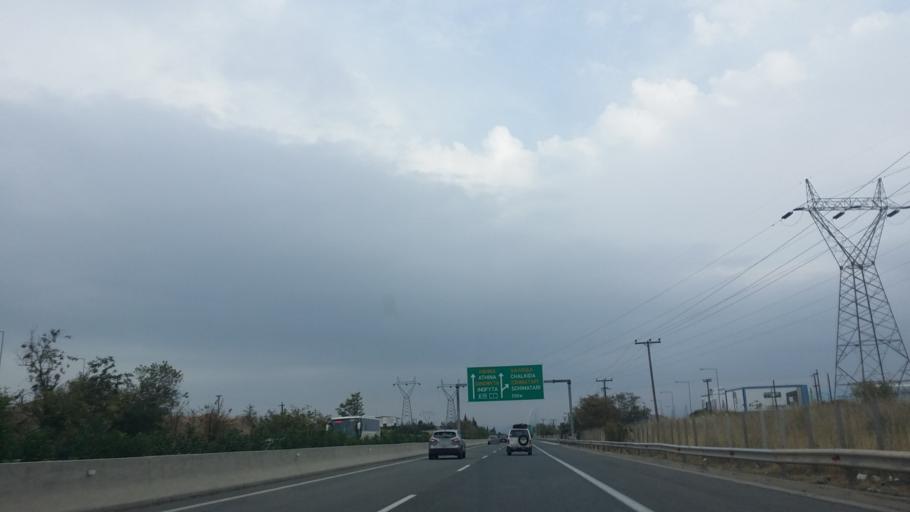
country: GR
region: Central Greece
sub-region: Nomos Voiotias
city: Schimatari
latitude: 38.3593
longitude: 23.5588
